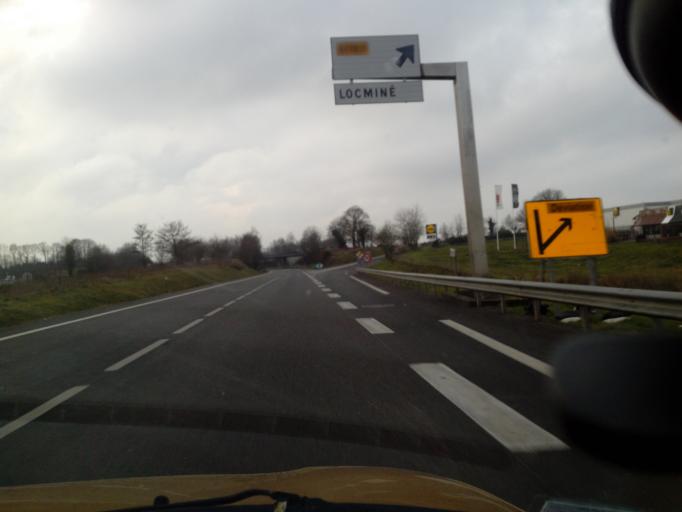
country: FR
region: Brittany
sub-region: Departement du Morbihan
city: Locmine
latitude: 47.8984
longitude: -2.8354
